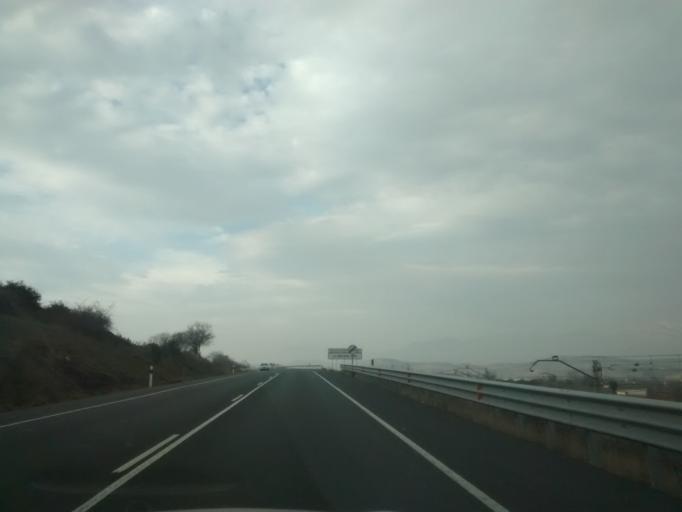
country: ES
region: La Rioja
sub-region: Provincia de La Rioja
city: Cenicero
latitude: 42.4862
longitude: -2.6577
